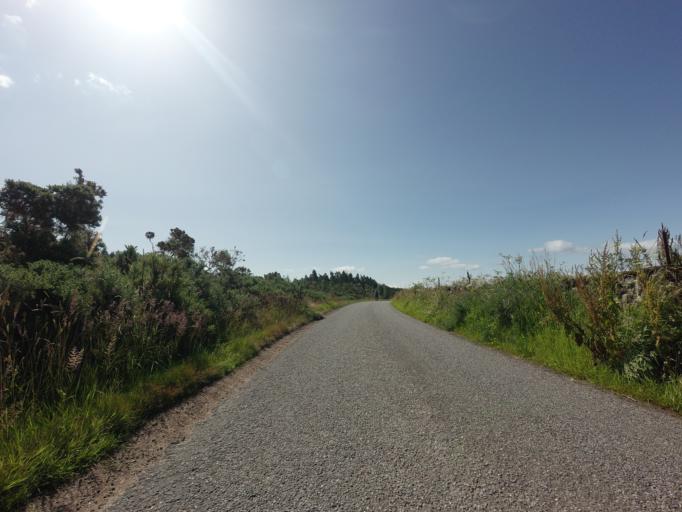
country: GB
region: Scotland
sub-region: Highland
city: Nairn
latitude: 57.5301
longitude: -3.8618
